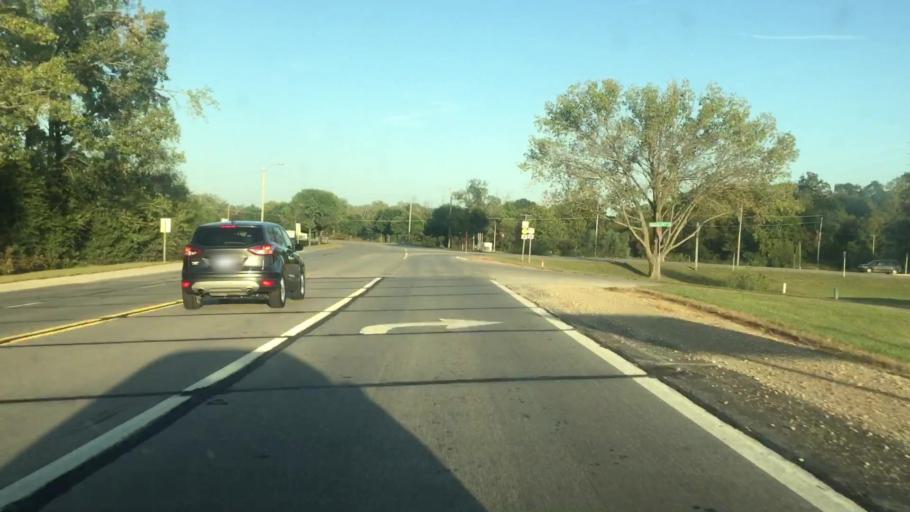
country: US
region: Kansas
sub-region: Atchison County
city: Atchison
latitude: 39.5559
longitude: -95.1542
